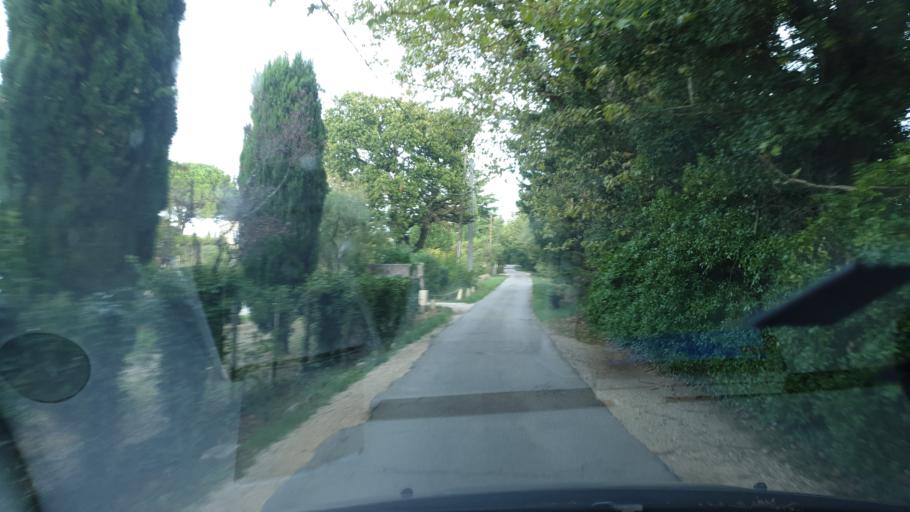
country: FR
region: Provence-Alpes-Cote d'Azur
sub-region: Departement du Vaucluse
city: Monteux
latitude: 44.0475
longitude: 5.0049
